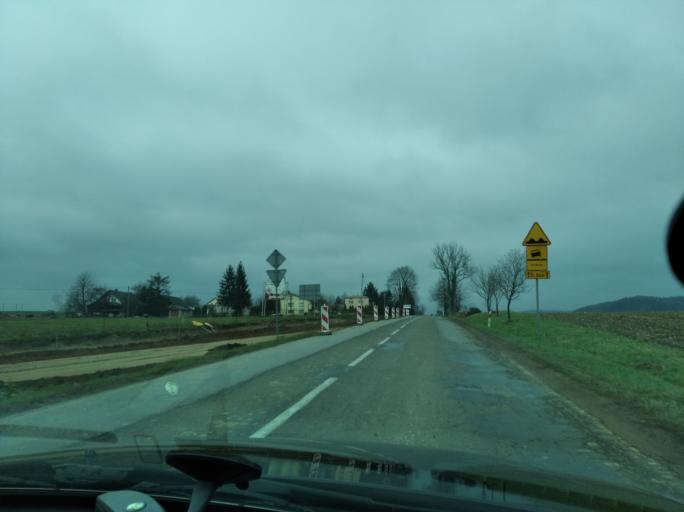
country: PL
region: Subcarpathian Voivodeship
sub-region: Powiat rzeszowski
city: Dynow
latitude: 49.8361
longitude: 22.2434
